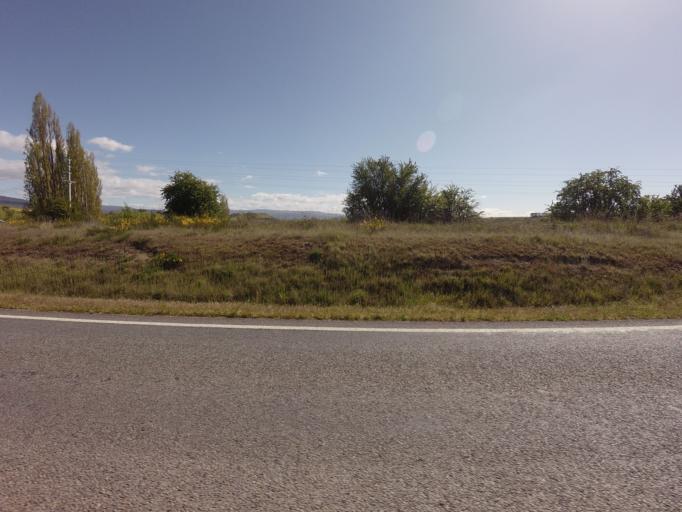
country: AU
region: Tasmania
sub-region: Derwent Valley
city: New Norfolk
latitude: -42.6878
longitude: 146.9420
